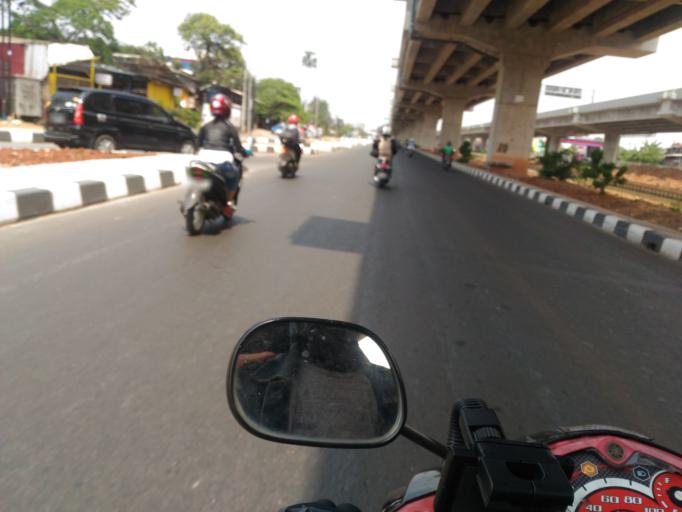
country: ID
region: West Java
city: Bekasi
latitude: -6.2479
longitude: 106.9246
